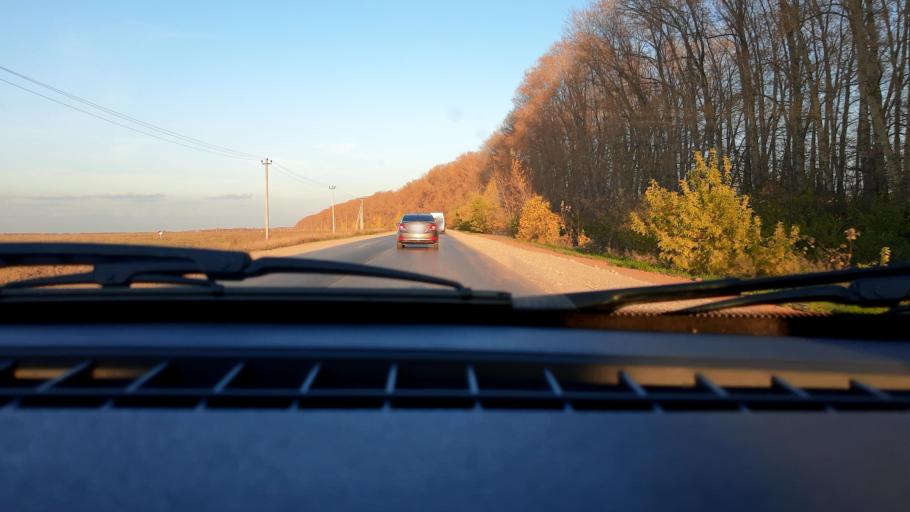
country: RU
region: Bashkortostan
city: Asanovo
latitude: 54.8171
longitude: 55.5992
